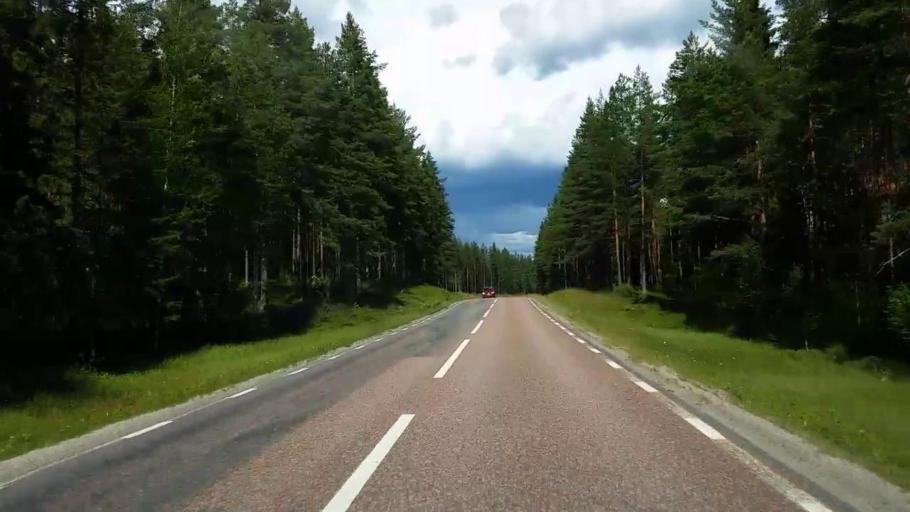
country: SE
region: Gaevleborg
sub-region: Ovanakers Kommun
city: Edsbyn
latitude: 61.3185
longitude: 15.5110
